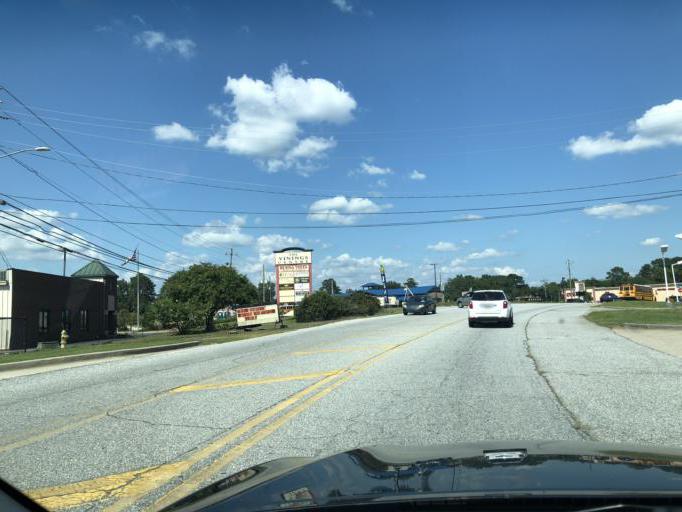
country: US
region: Georgia
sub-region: Muscogee County
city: Columbus
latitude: 32.5217
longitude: -84.9172
